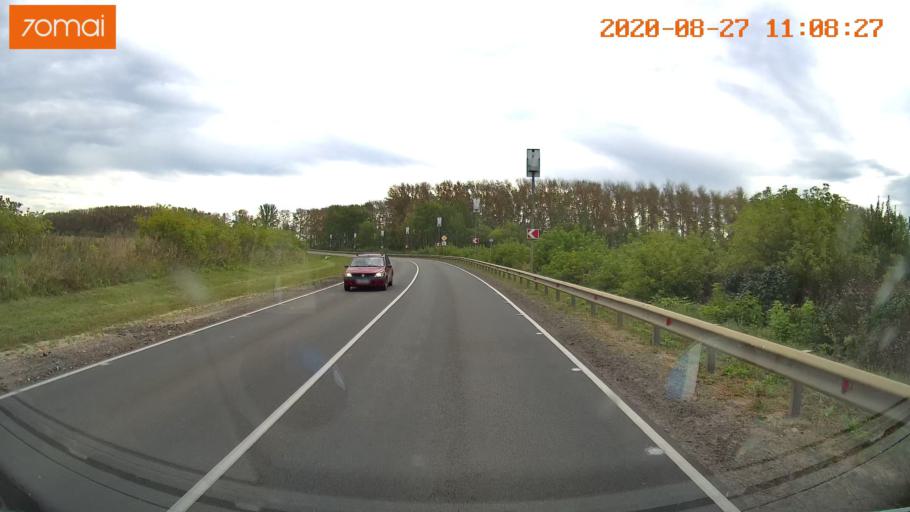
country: RU
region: Rjazan
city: Oktyabr'skiy
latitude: 54.1412
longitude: 38.6900
